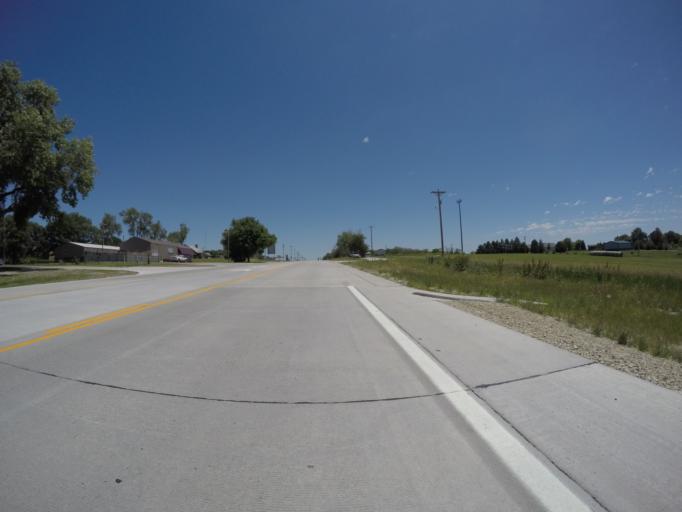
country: US
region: Kansas
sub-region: Republic County
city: Belleville
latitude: 39.8125
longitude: -97.6358
